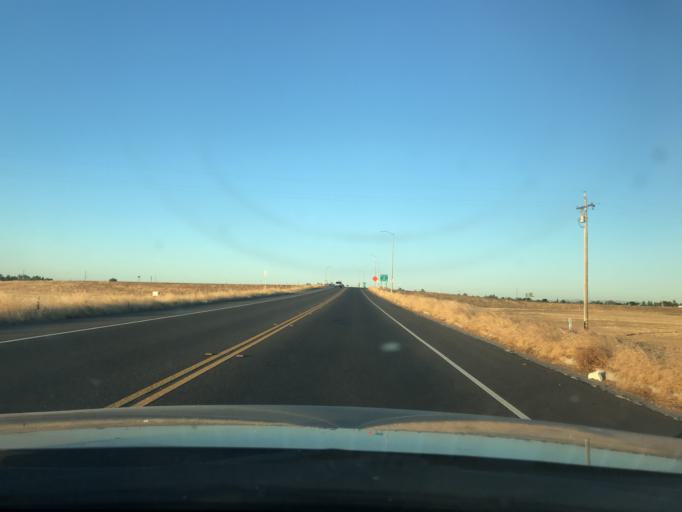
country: US
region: California
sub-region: Merced County
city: Atwater
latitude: 37.3361
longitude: -120.5658
